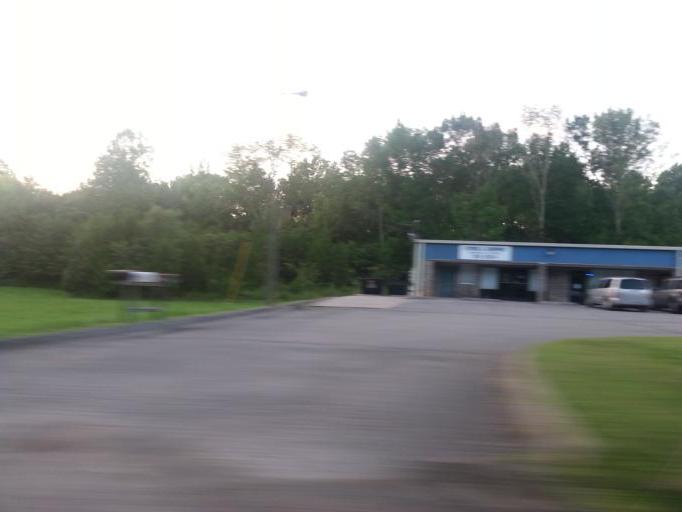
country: US
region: Tennessee
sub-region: Union County
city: Condon
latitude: 36.1950
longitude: -83.7701
